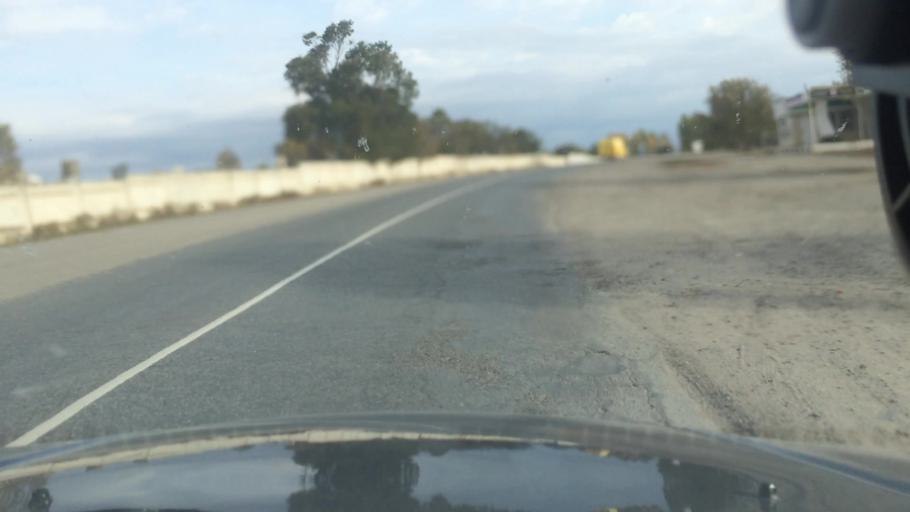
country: KG
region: Ysyk-Koel
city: Karakol
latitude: 42.5368
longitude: 78.3820
